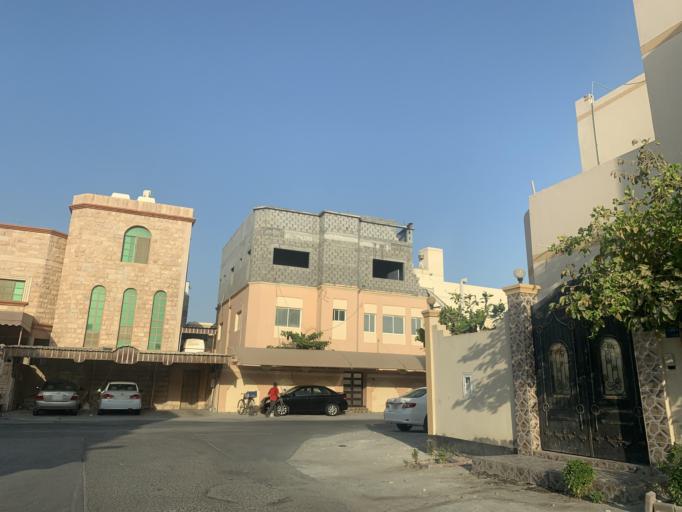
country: BH
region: Muharraq
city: Al Muharraq
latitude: 26.2873
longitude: 50.6274
